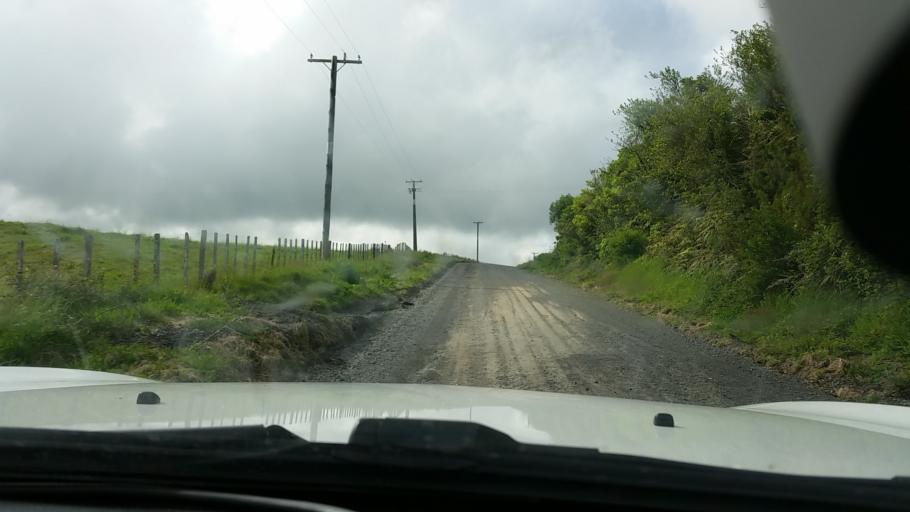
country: NZ
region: Bay of Plenty
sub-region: Rotorua District
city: Rotorua
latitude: -38.1474
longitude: 176.0824
